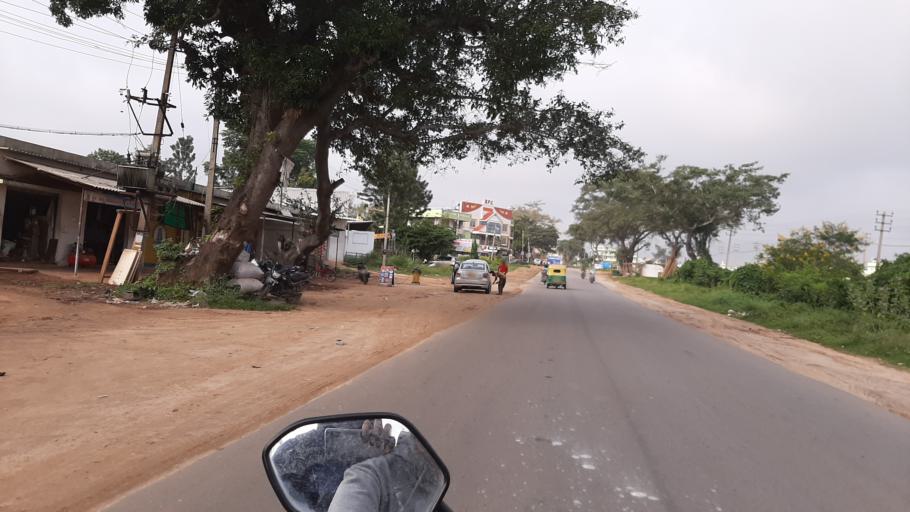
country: IN
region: Karnataka
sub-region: Bangalore Rural
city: Nelamangala
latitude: 12.9759
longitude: 77.4252
